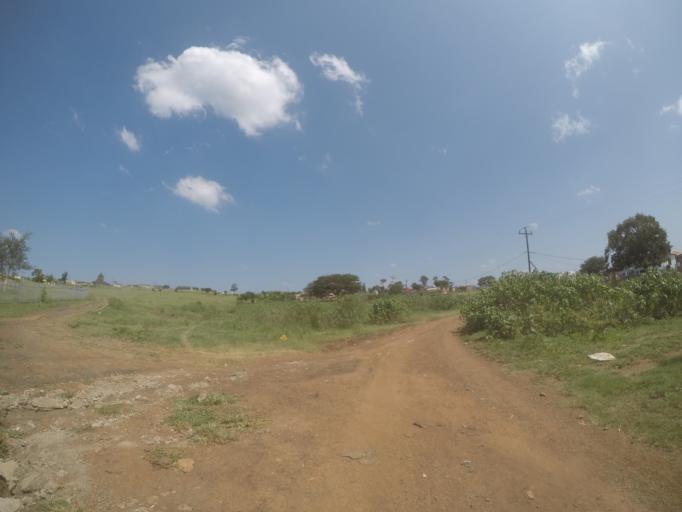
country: ZA
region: KwaZulu-Natal
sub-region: uThungulu District Municipality
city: Empangeni
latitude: -28.5906
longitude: 31.7402
